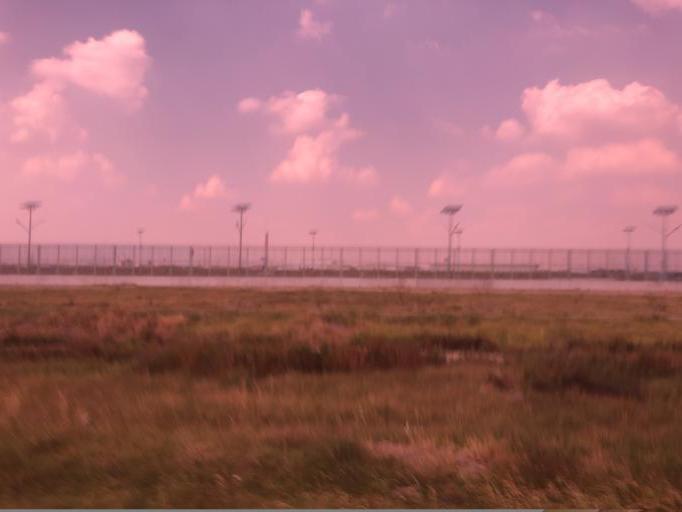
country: MX
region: Mexico
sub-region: Ciudad Nezahualcoyotl
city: Poligonos
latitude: 19.4769
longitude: -98.9844
